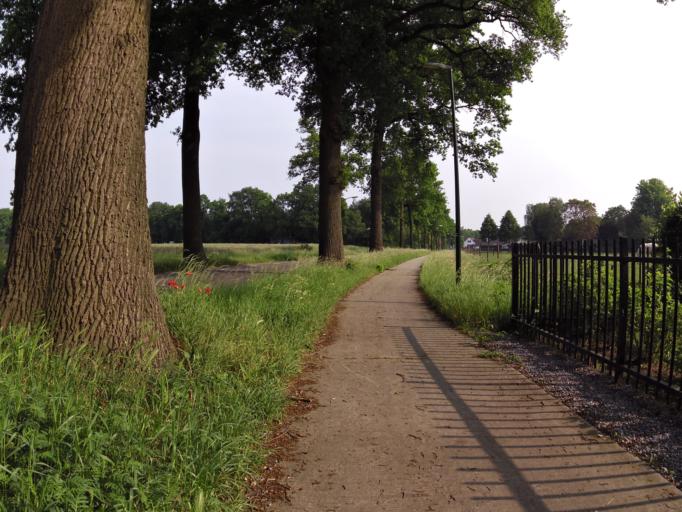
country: NL
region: North Brabant
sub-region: Gemeente Haaren
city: Haaren
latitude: 51.6580
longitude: 5.2191
